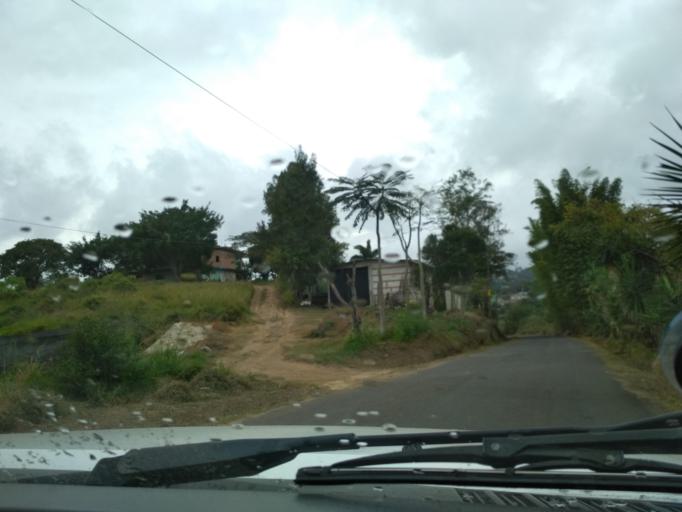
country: MX
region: Veracruz
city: El Castillo
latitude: 19.5342
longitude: -96.8143
